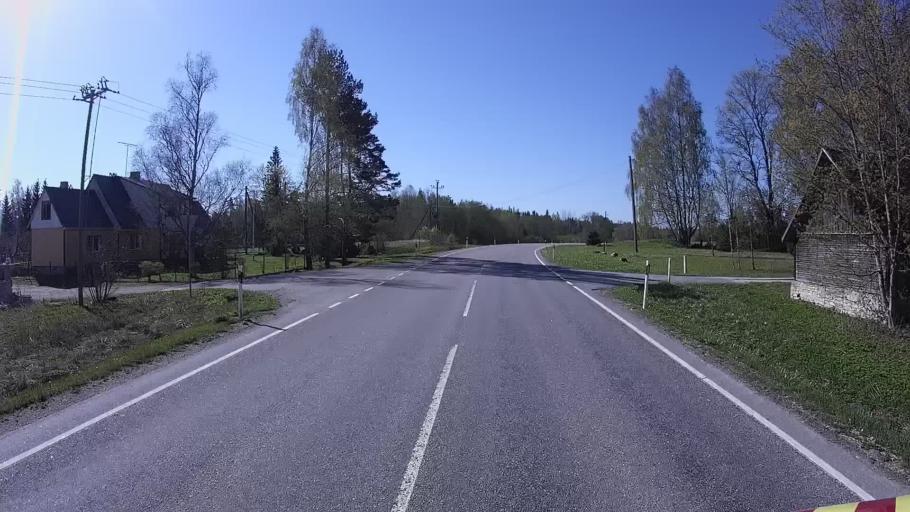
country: EE
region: Raplamaa
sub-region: Rapla vald
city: Rapla
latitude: 58.9618
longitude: 24.7673
